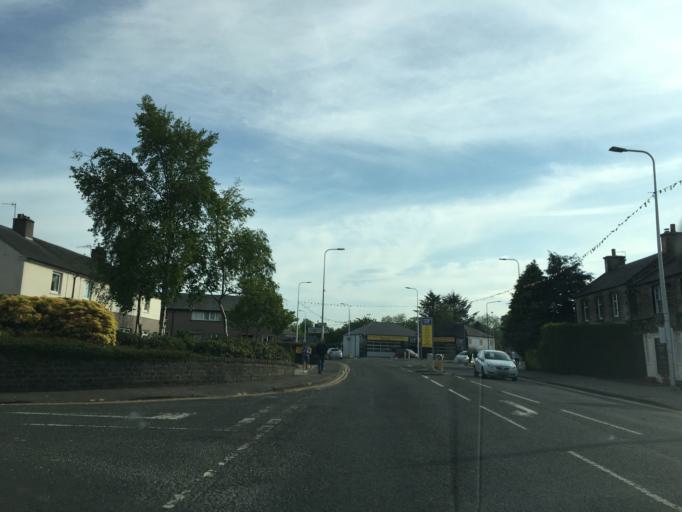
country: GB
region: Scotland
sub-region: Midlothian
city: Penicuik
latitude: 55.8324
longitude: -3.2235
